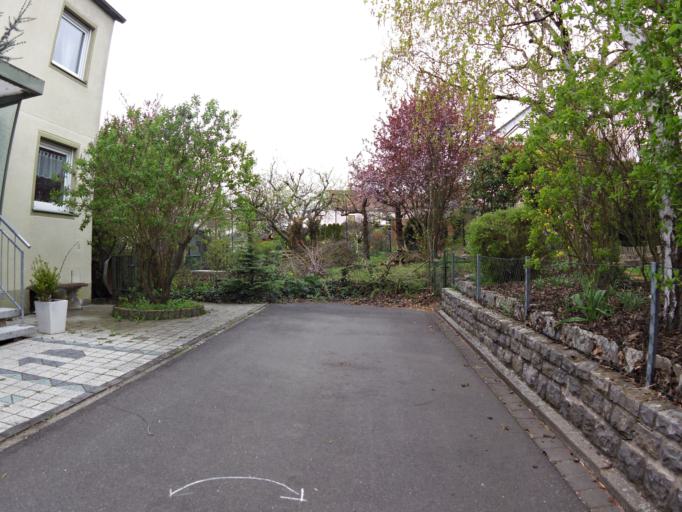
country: DE
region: Bavaria
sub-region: Regierungsbezirk Unterfranken
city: Rottendorf
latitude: 49.7964
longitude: 10.0225
